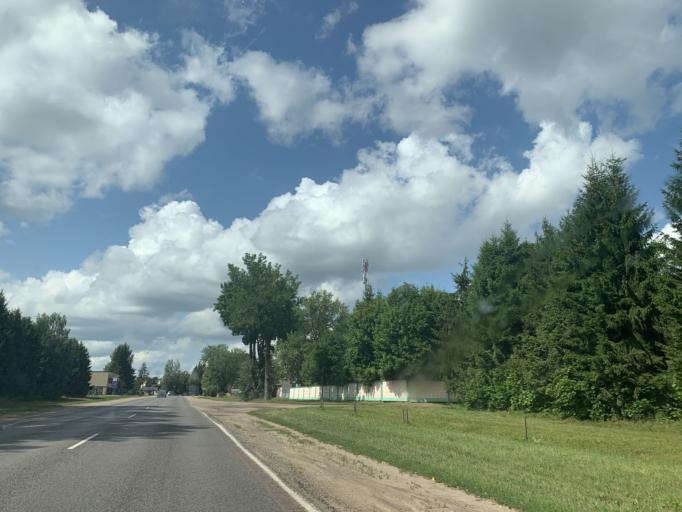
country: BY
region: Minsk
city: Enyerhyetykaw
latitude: 53.5828
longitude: 27.0541
